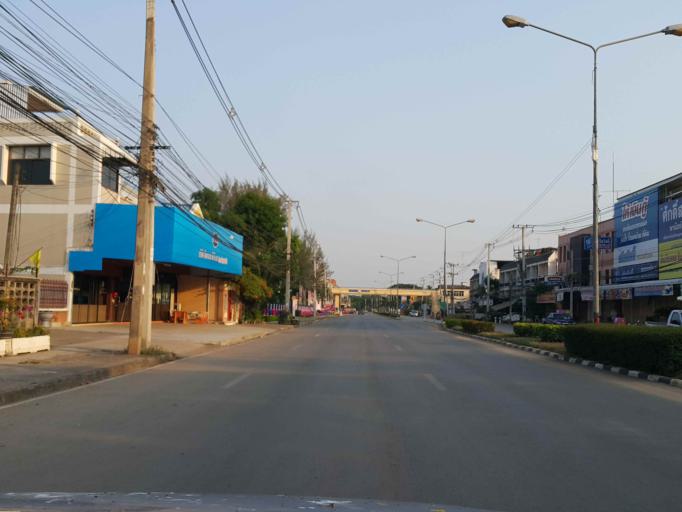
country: TH
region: Sukhothai
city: Sawankhalok
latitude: 17.2969
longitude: 99.8363
